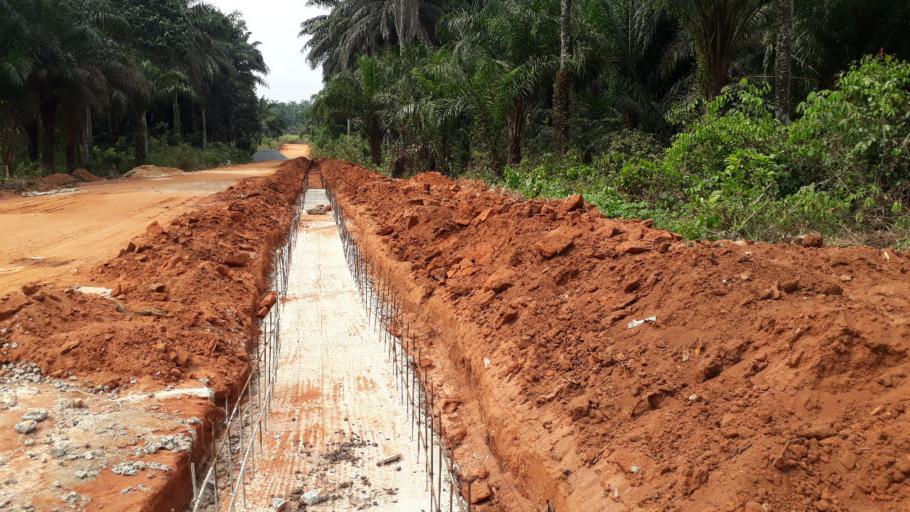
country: NG
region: Imo
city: Ihuo
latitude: 5.5719
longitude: 7.2636
